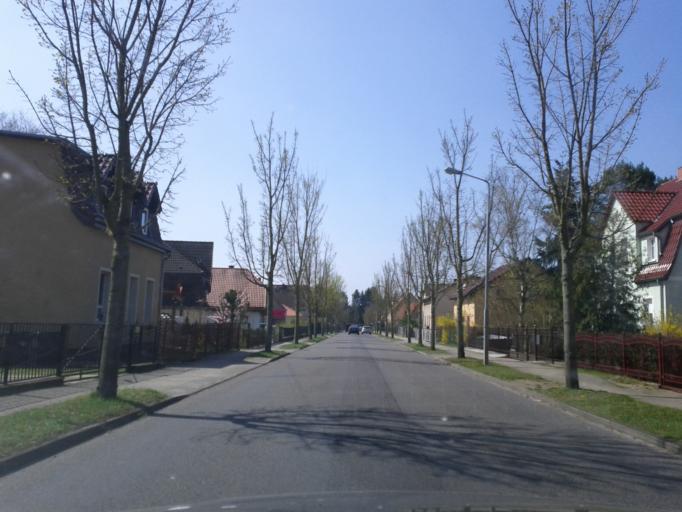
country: DE
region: Brandenburg
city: Grunheide
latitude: 52.4165
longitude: 13.8129
